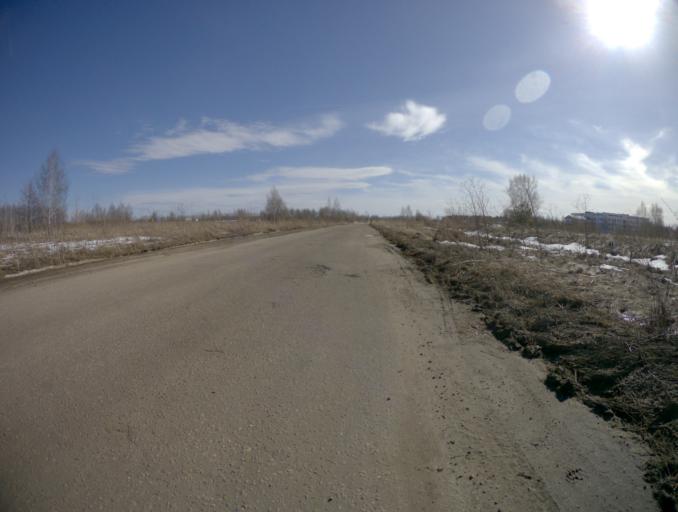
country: RU
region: Vladimir
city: Suzdal'
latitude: 56.4401
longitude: 40.4643
